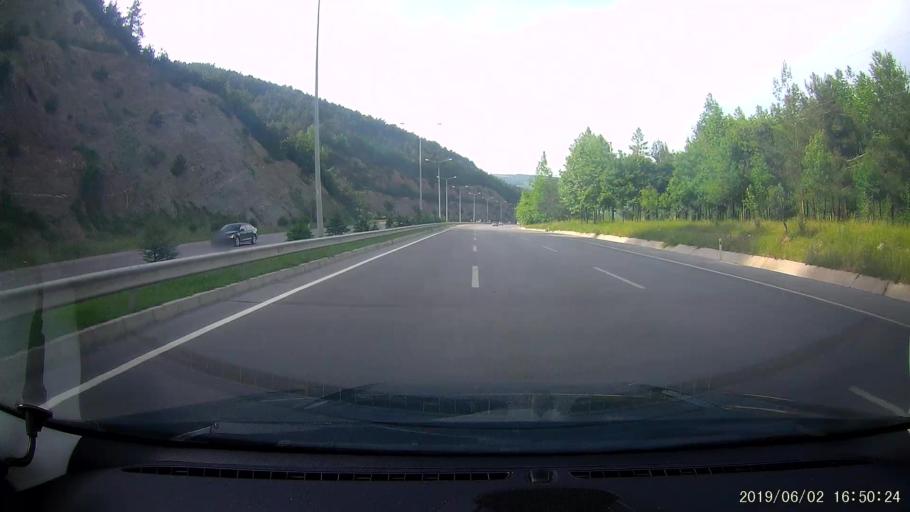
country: TR
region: Samsun
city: Samsun
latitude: 41.2540
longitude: 36.1736
